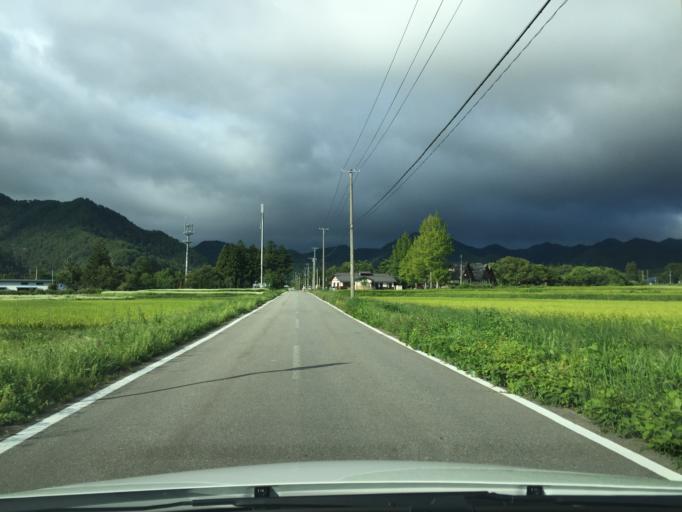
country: JP
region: Yamagata
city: Takahata
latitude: 37.9477
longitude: 140.2051
